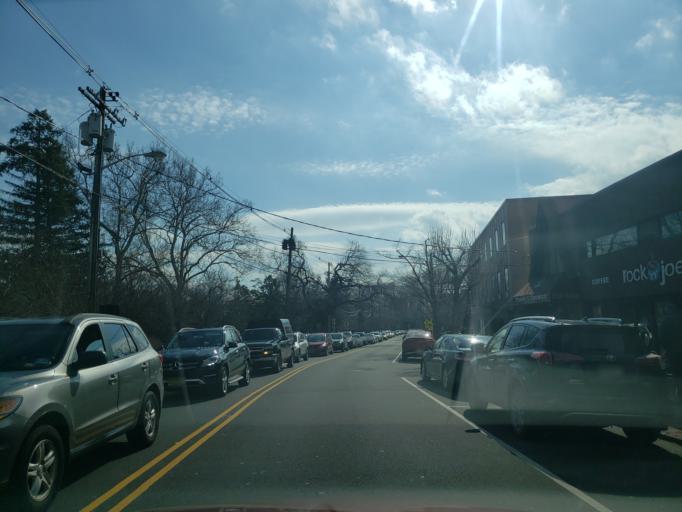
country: US
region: New Jersey
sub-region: Union County
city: Springfield
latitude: 40.7235
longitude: -74.3071
